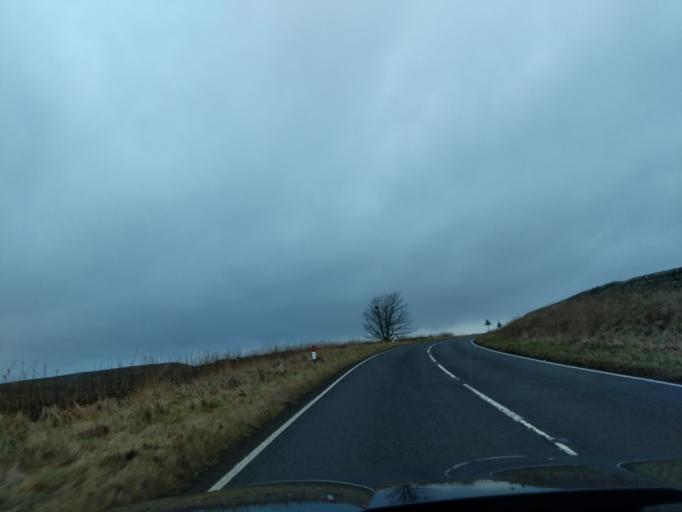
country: GB
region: England
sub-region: Northumberland
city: Corsenside
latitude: 55.1921
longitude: -2.0689
